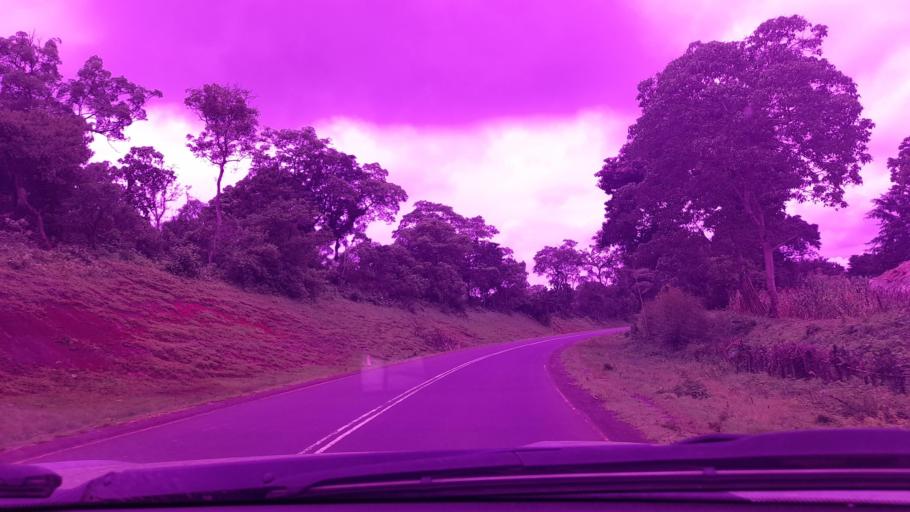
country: ET
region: Southern Nations, Nationalities, and People's Region
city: Bonga
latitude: 7.2798
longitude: 35.9530
